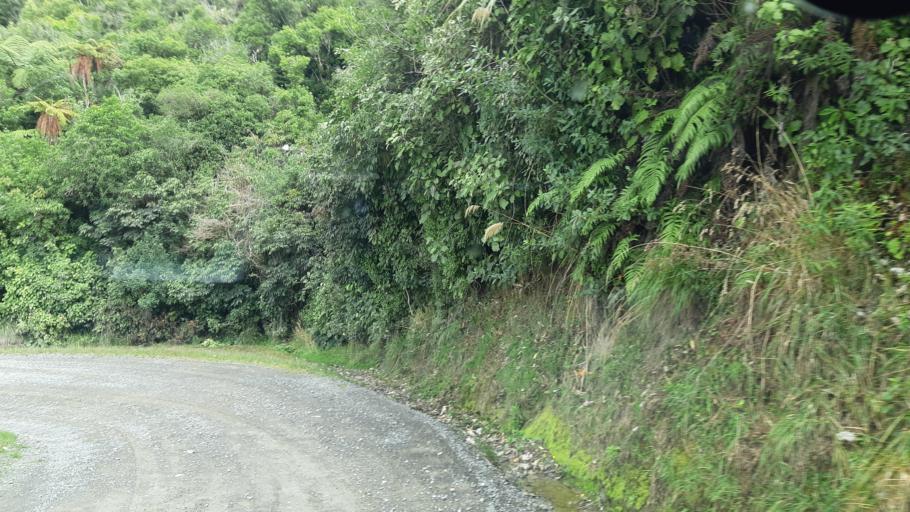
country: NZ
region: Manawatu-Wanganui
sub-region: Ruapehu District
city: Waiouru
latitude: -39.7928
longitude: 175.6757
